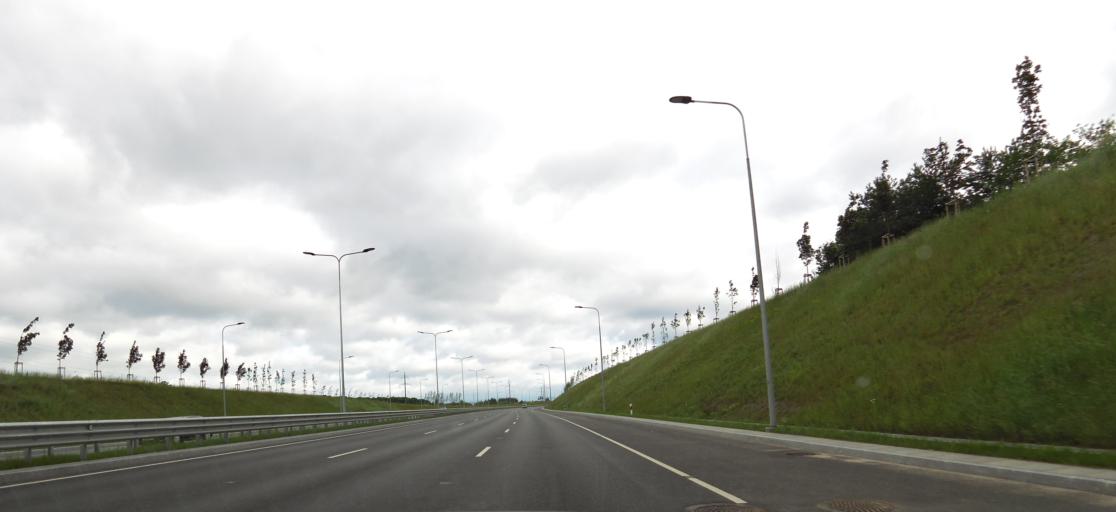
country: LT
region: Vilnius County
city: Justiniskes
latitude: 54.7093
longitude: 25.2098
